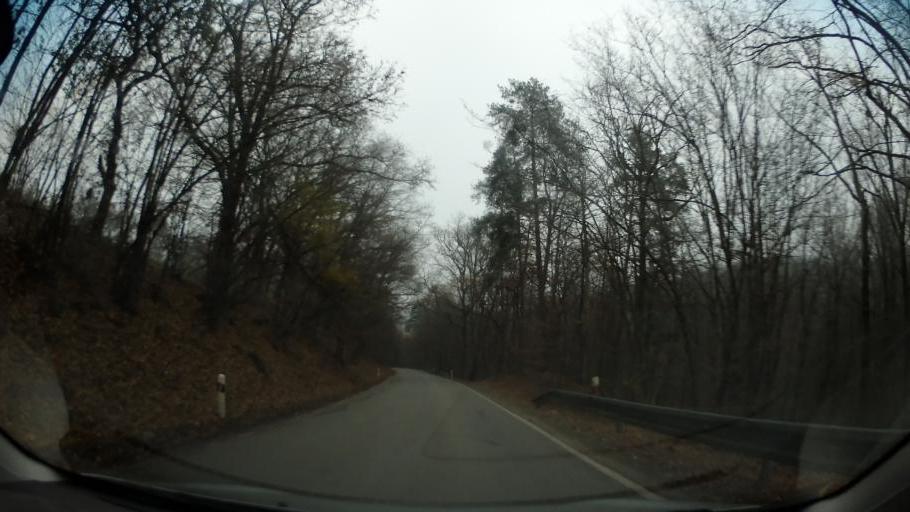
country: CZ
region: Vysocina
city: Mohelno
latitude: 49.1444
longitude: 16.1996
